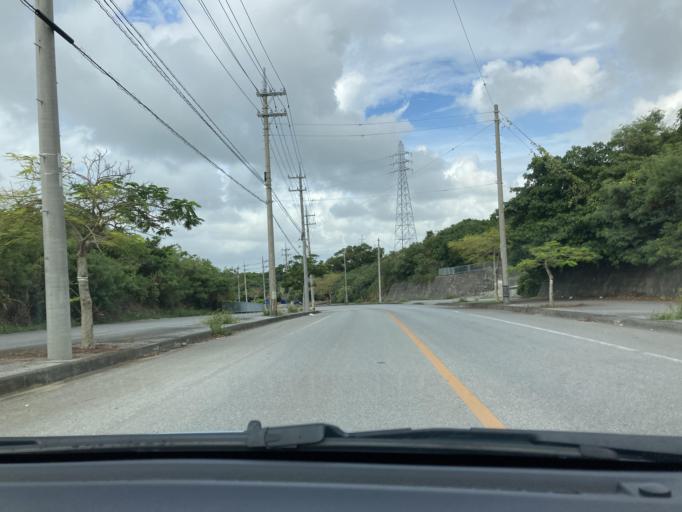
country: JP
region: Okinawa
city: Itoman
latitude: 26.1215
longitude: 127.6926
